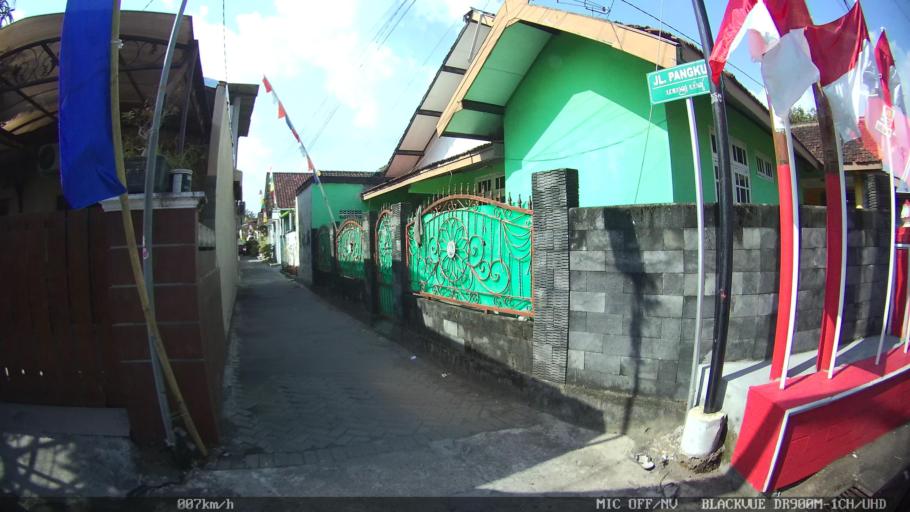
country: ID
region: Daerah Istimewa Yogyakarta
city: Yogyakarta
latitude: -7.8290
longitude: 110.3915
